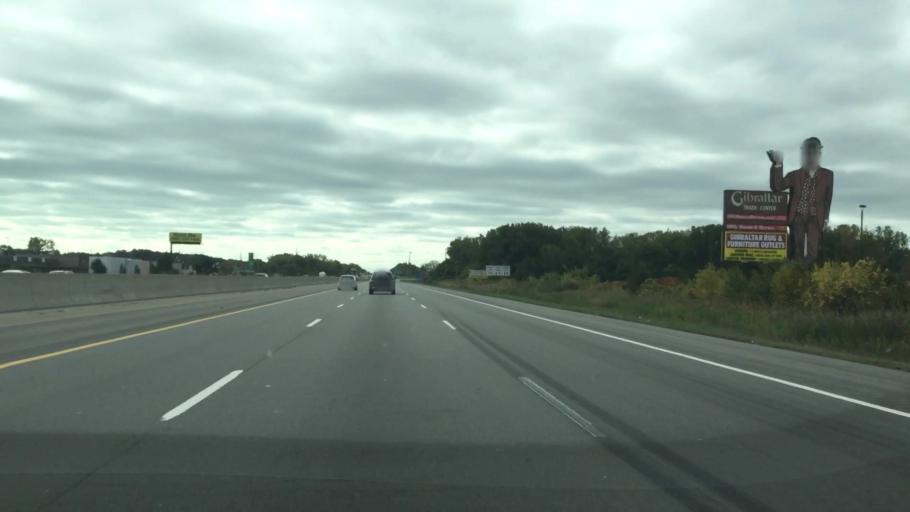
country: US
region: Michigan
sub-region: Macomb County
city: Mount Clemens
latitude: 42.6019
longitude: -82.8538
